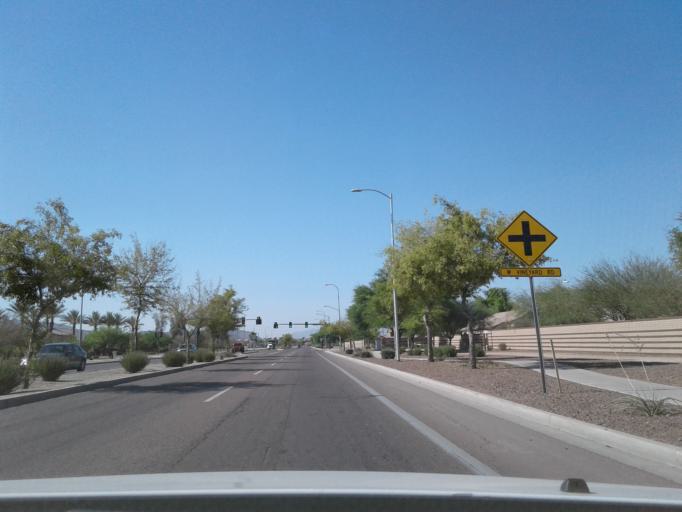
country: US
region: Arizona
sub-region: Maricopa County
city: Laveen
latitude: 33.3860
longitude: -112.1683
